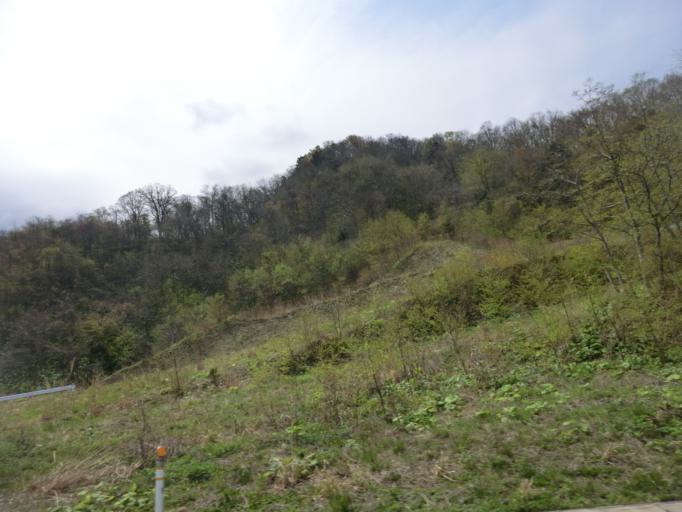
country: JP
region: Aomori
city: Mutsu
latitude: 41.3620
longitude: 140.8312
